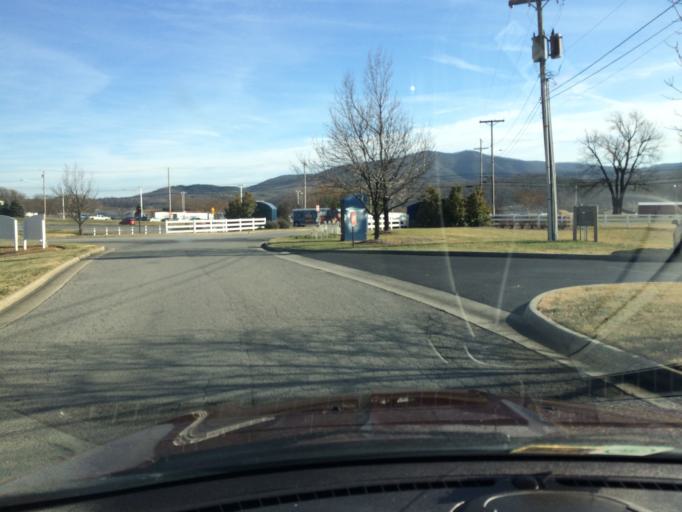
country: US
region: Virginia
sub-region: City of Salem
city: Salem
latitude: 37.2783
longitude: -80.1268
